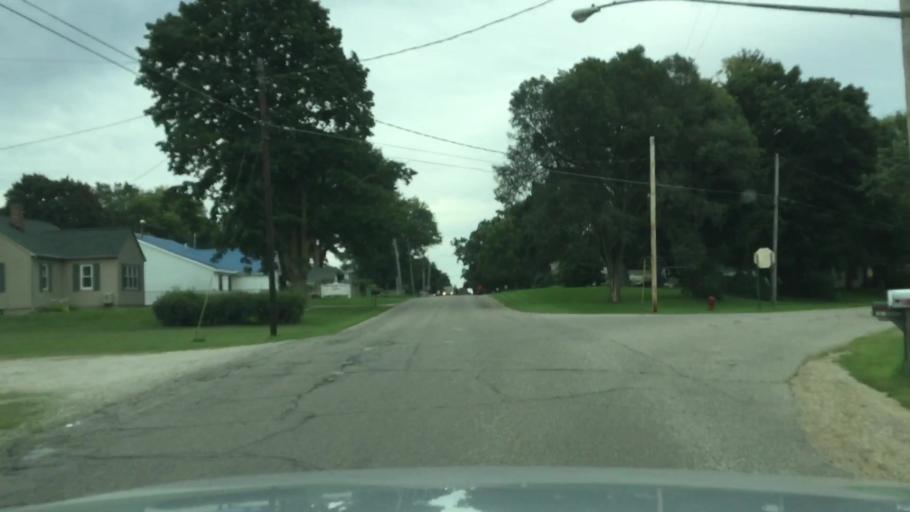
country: US
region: Michigan
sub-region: Shiawassee County
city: Durand
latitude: 42.8800
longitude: -84.0652
